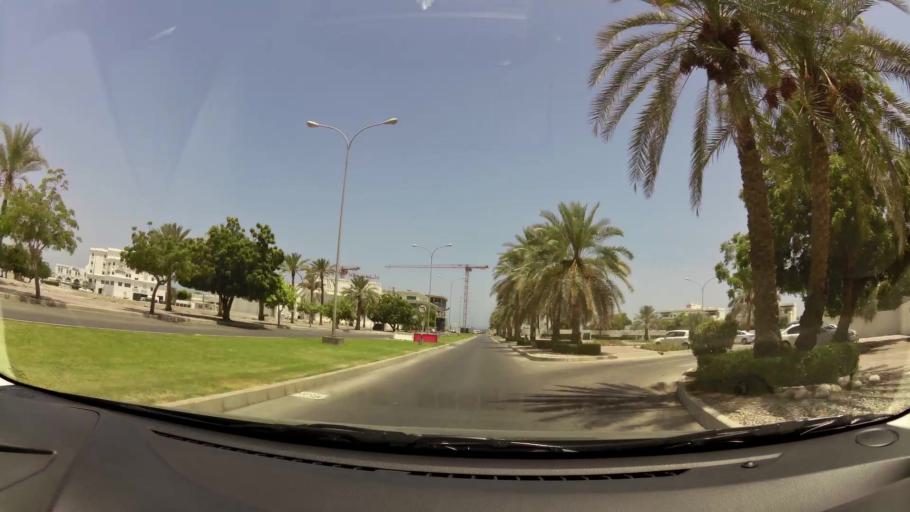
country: OM
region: Muhafazat Masqat
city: Bawshar
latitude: 23.6104
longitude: 58.4551
